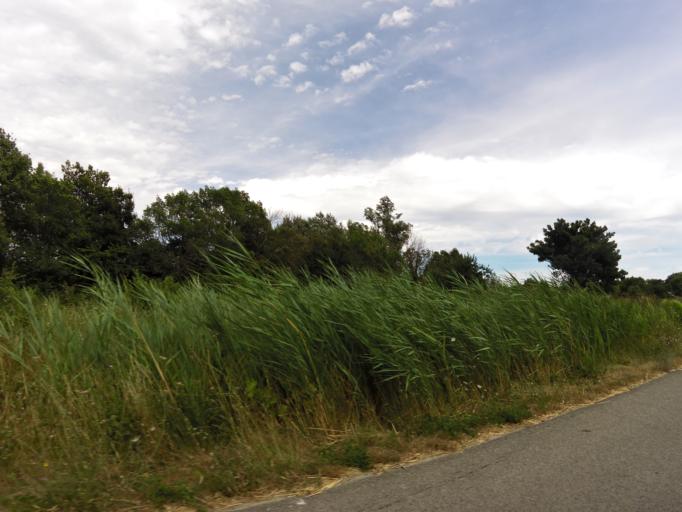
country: FR
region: Languedoc-Roussillon
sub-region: Departement du Gard
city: Saint-Mamert-du-Gard
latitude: 43.8860
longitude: 4.1946
